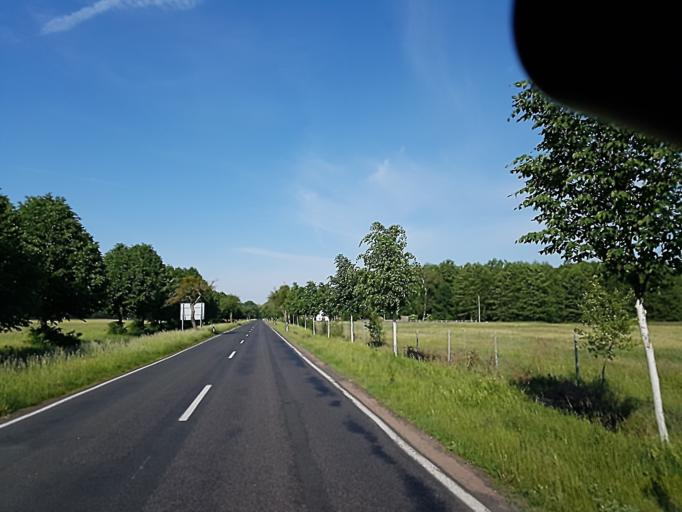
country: DE
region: Saxony-Anhalt
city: Klieken
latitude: 51.9610
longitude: 12.3441
